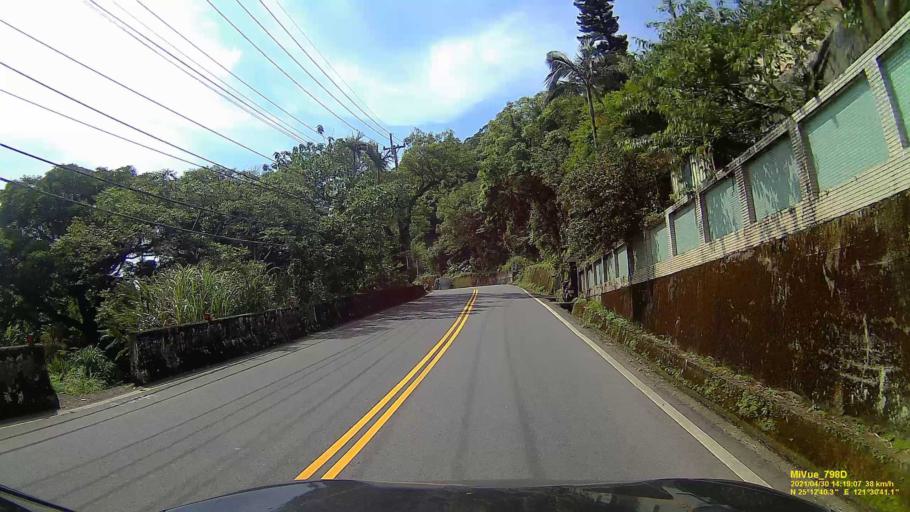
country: TW
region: Taipei
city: Taipei
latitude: 25.2114
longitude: 121.5113
